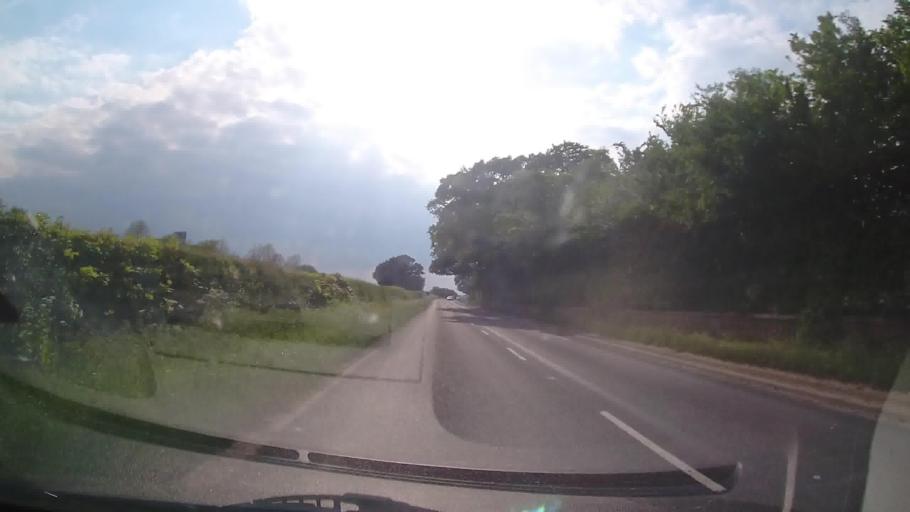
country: GB
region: England
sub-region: Telford and Wrekin
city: Wellington
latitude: 52.6924
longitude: -2.5449
